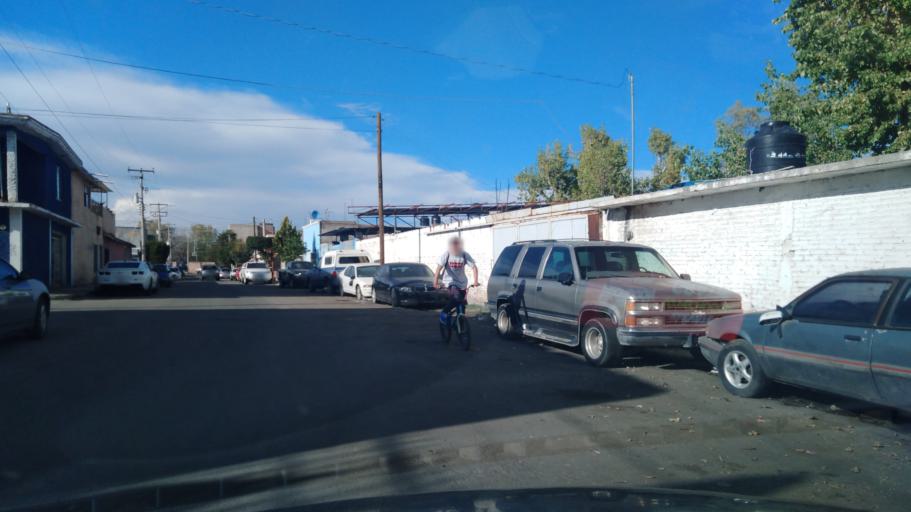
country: MX
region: Durango
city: Victoria de Durango
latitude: 24.0186
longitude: -104.6361
